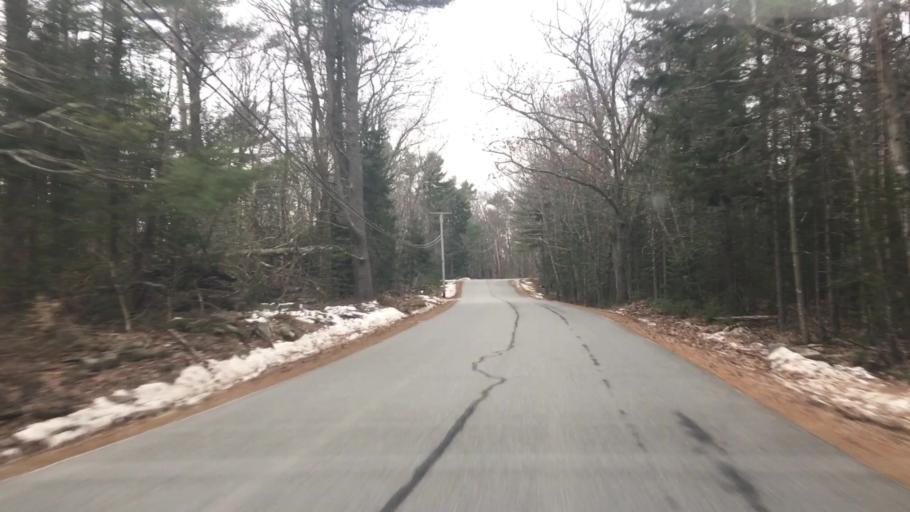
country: US
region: Maine
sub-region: Cumberland County
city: Freeport
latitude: 43.8418
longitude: -70.0717
